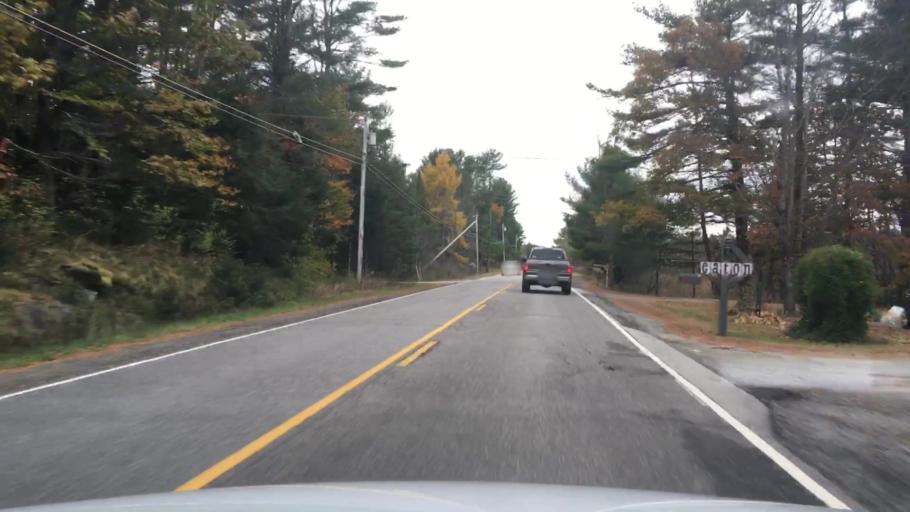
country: US
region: Maine
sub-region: Sagadahoc County
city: Richmond
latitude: 44.1294
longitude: -69.9146
